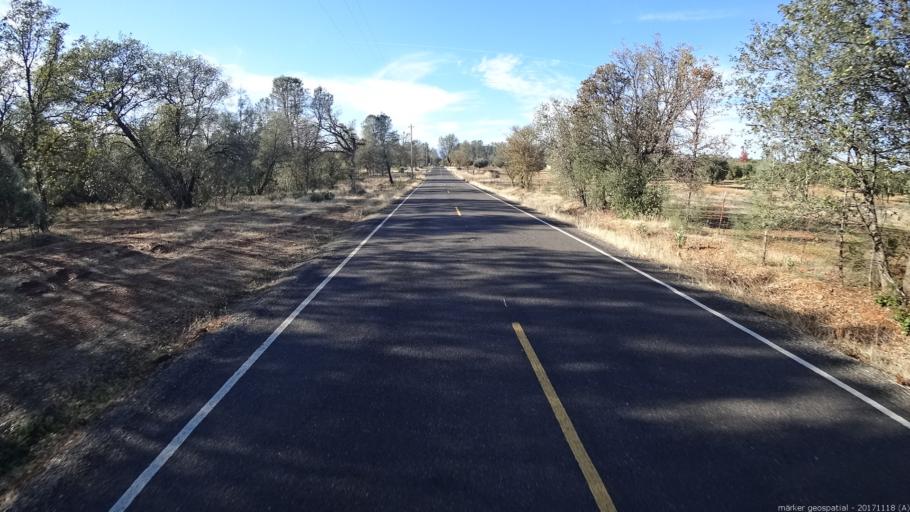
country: US
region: California
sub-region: Shasta County
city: Redding
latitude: 40.4502
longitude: -122.4514
